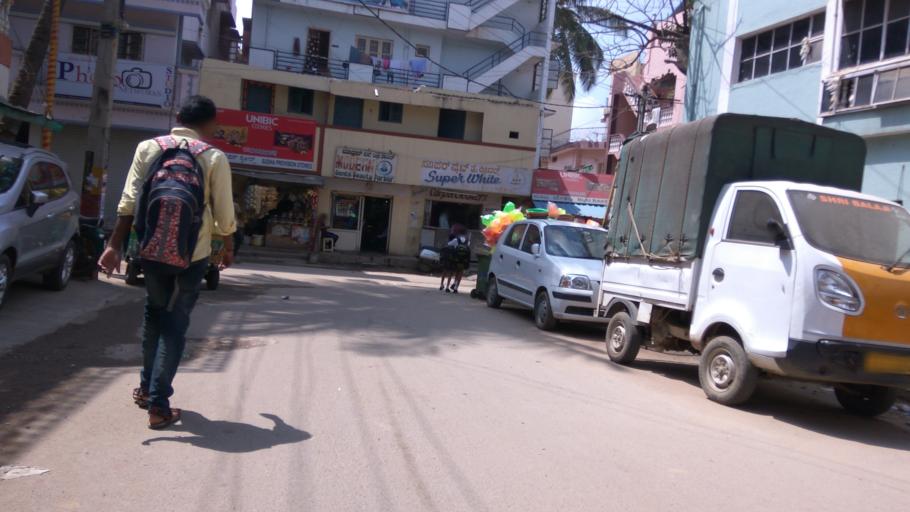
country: IN
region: Karnataka
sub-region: Bangalore Urban
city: Bangalore
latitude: 12.9747
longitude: 77.6391
